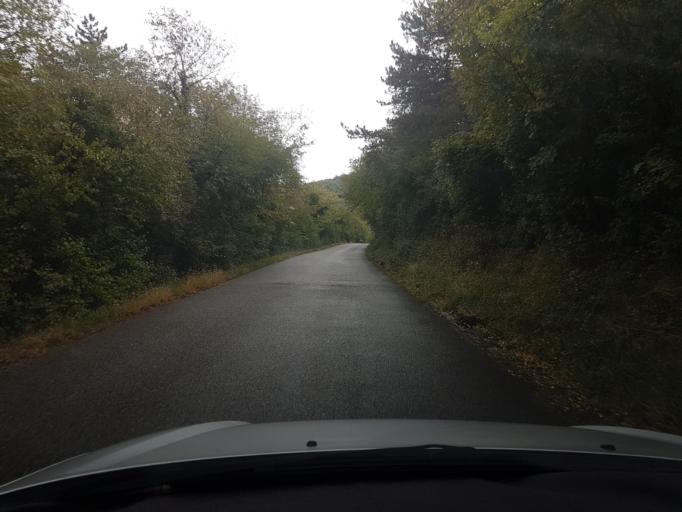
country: IT
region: Friuli Venezia Giulia
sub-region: Provincia di Gorizia
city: Doberdo del Lago
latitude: 45.8286
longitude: 13.5620
